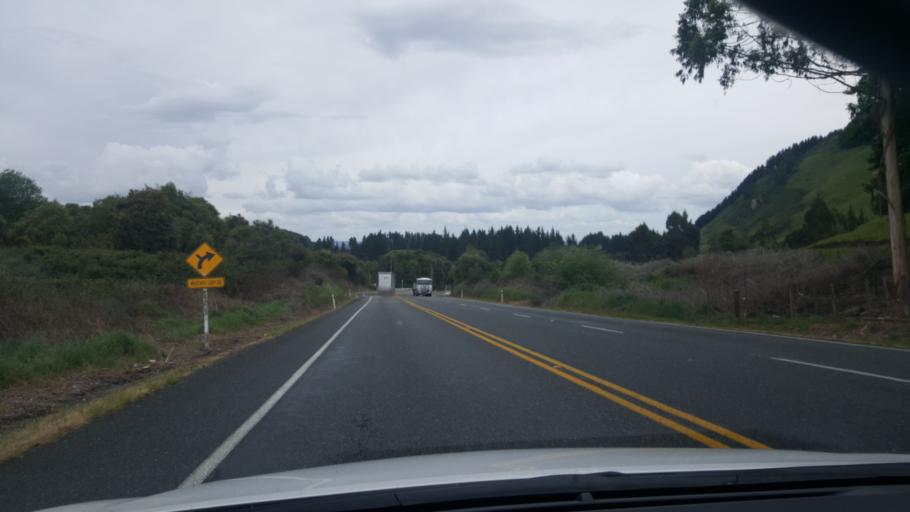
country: NZ
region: Bay of Plenty
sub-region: Rotorua District
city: Rotorua
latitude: -38.3504
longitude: 176.3614
